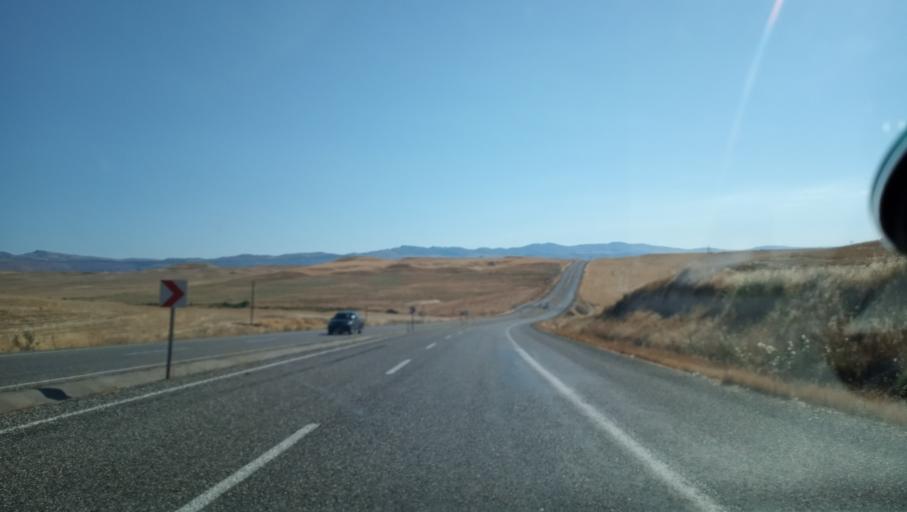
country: TR
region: Diyarbakir
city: Bagdere
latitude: 38.1246
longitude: 40.7457
